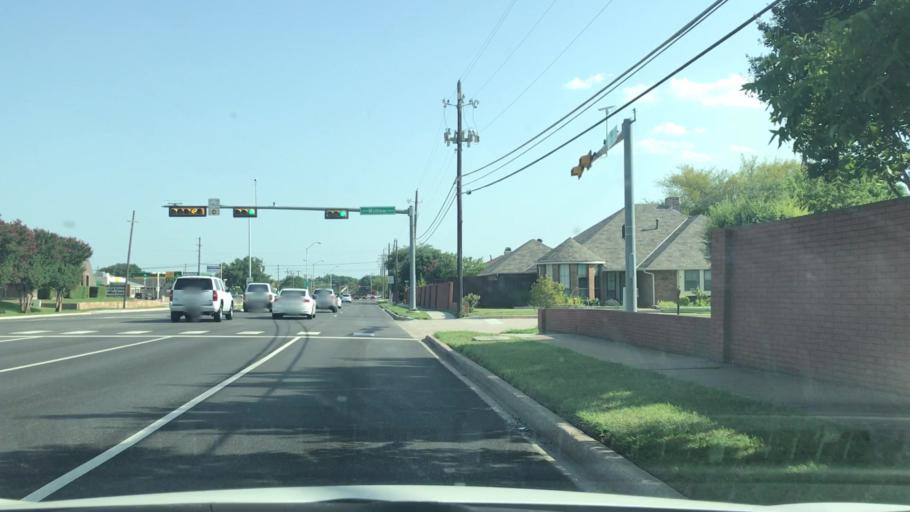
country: US
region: Texas
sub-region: Collin County
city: Plano
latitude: 33.0228
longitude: -96.7500
